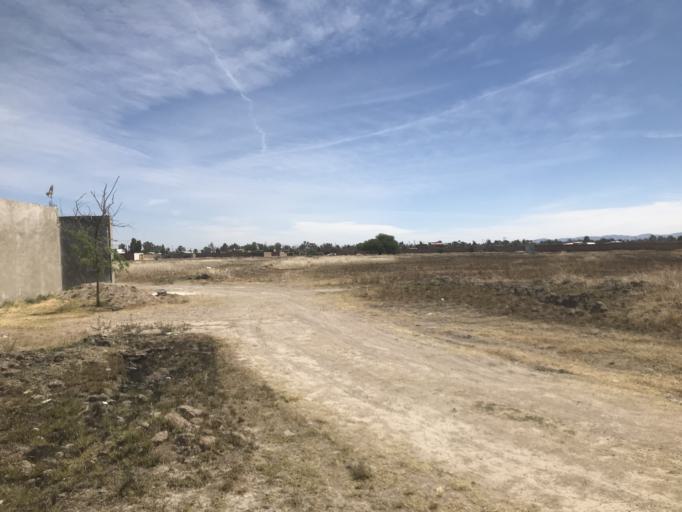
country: MX
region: Durango
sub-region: Durango
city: Sebastian Lerdo de Tejada
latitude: 23.9777
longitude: -104.6564
